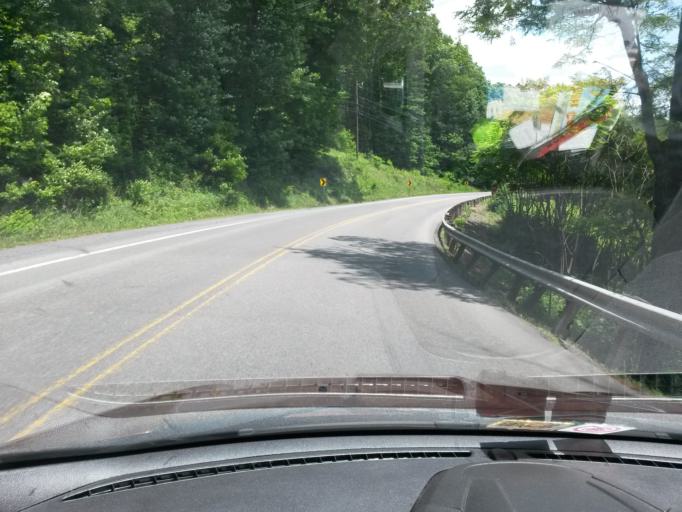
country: US
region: West Virginia
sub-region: Greenbrier County
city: Rainelle
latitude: 37.9187
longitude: -80.6409
